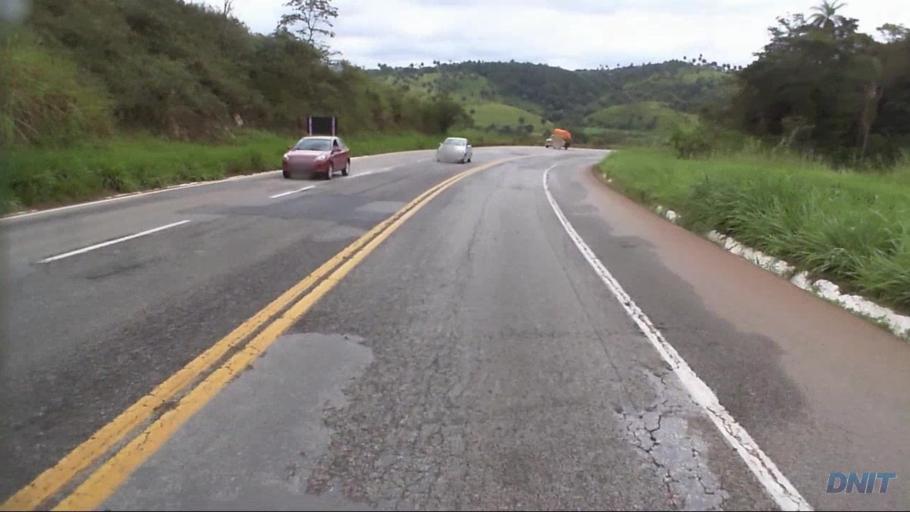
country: BR
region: Minas Gerais
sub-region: Barao De Cocais
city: Barao de Cocais
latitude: -19.8192
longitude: -43.3922
